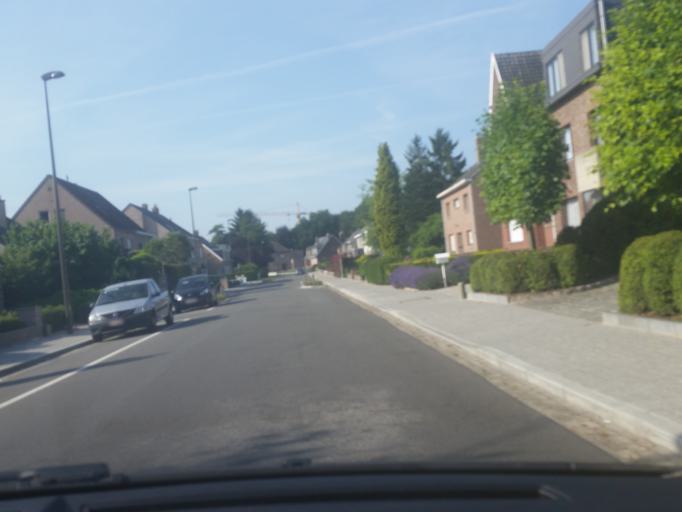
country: BE
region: Flanders
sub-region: Provincie Antwerpen
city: Mechelen
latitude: 51.0089
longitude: 4.4690
